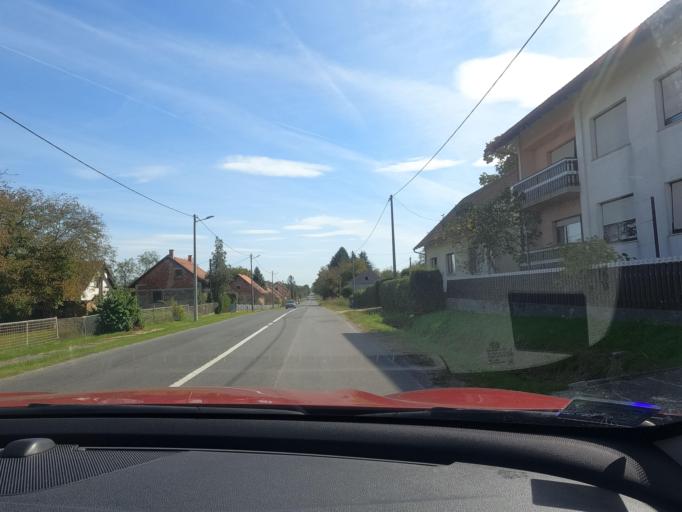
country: HR
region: Sisacko-Moslavacka
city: Petrinja
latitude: 45.4430
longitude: 16.3240
